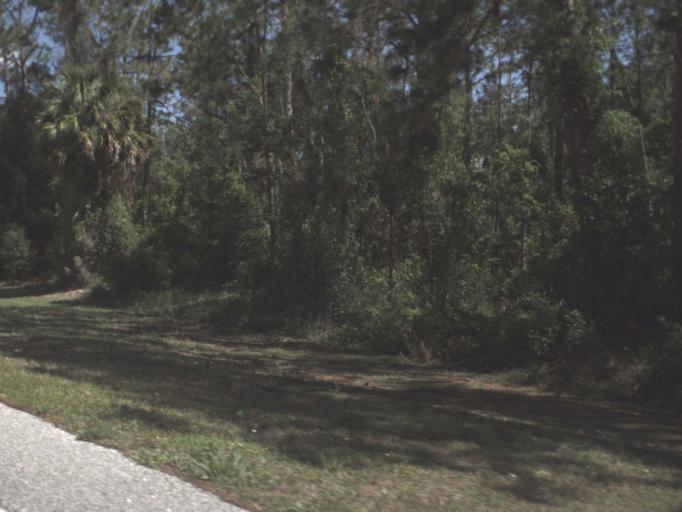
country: US
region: Florida
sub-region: Flagler County
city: Palm Coast
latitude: 29.5548
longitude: -81.2659
